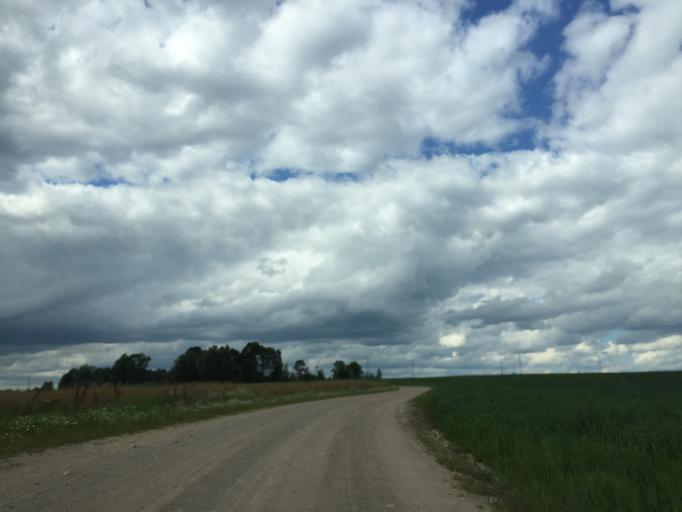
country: LV
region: Malpils
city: Malpils
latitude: 56.8505
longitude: 25.0488
